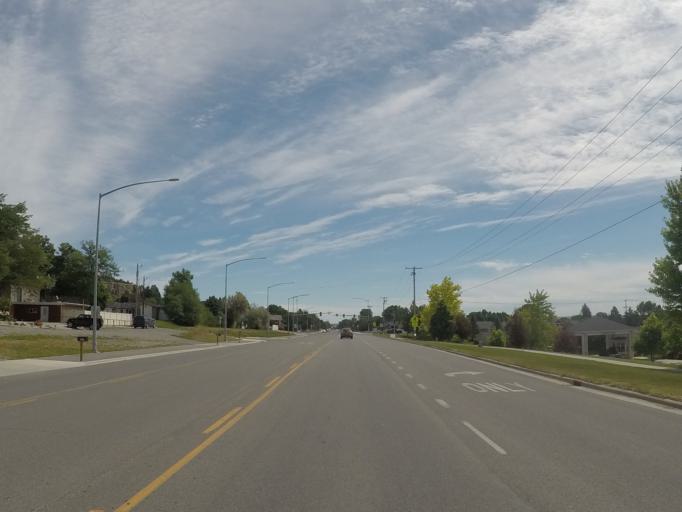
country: US
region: Montana
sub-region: Yellowstone County
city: Billings
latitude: 45.7985
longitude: -108.6140
